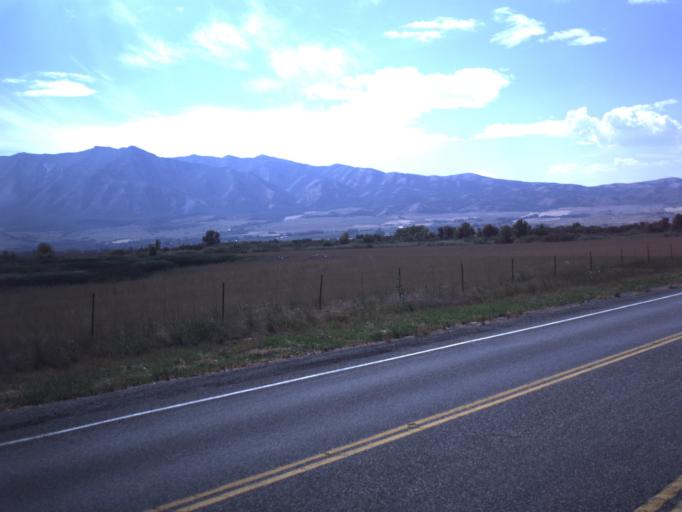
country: US
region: Utah
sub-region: Cache County
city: Benson
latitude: 41.7422
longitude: -111.9138
